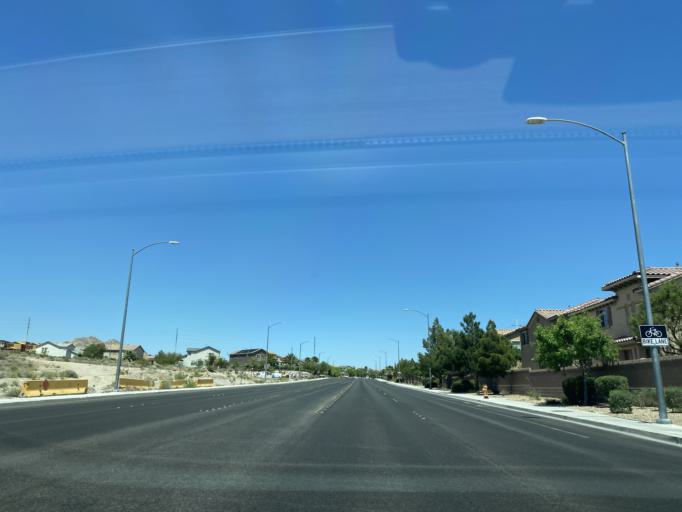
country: US
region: Nevada
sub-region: Clark County
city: Summerlin South
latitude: 36.2348
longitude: -115.3307
